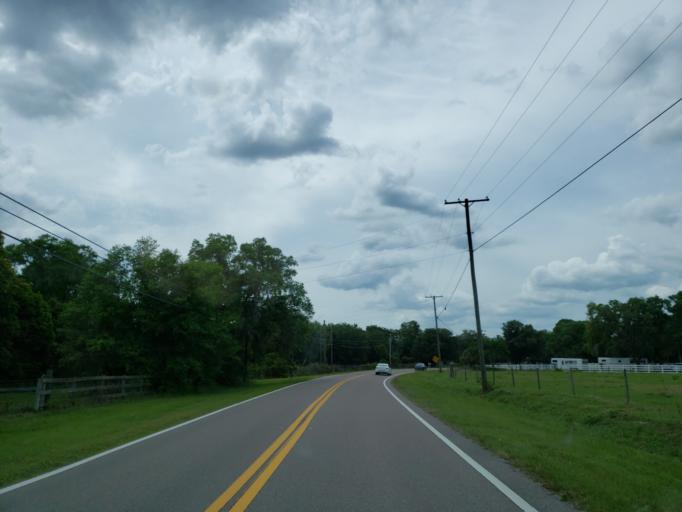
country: US
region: Florida
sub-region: Hillsborough County
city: Citrus Park
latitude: 28.1096
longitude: -82.6020
